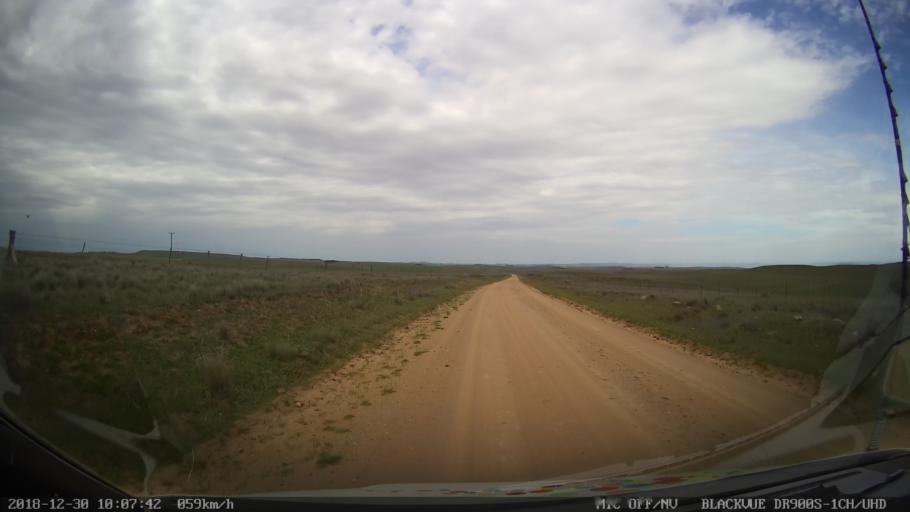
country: AU
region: New South Wales
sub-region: Cooma-Monaro
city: Cooma
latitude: -36.5413
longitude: 149.1202
